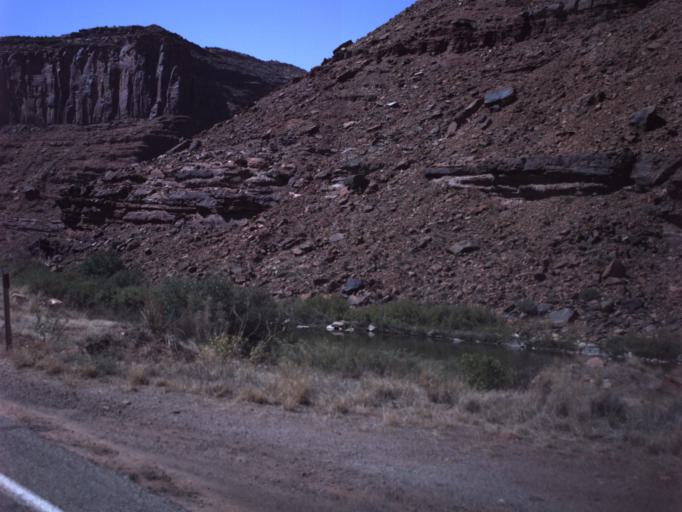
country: US
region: Utah
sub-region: Grand County
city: Moab
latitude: 38.6759
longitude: -109.4892
